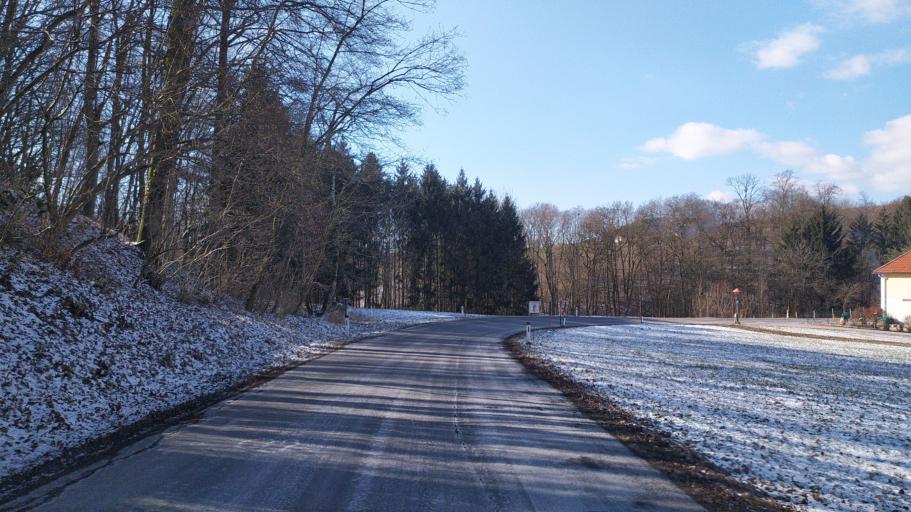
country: AT
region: Lower Austria
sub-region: Politischer Bezirk Amstetten
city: Zeillern
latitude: 48.1558
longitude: 14.7358
